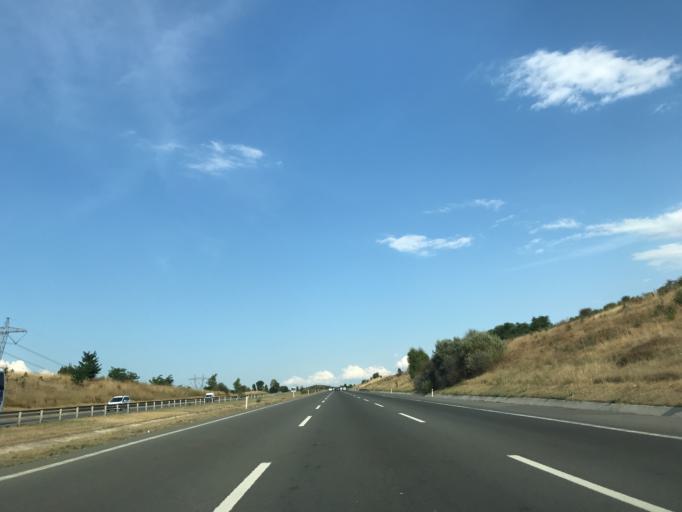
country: TR
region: Bolu
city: Yenicaga
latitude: 40.7646
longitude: 32.0442
